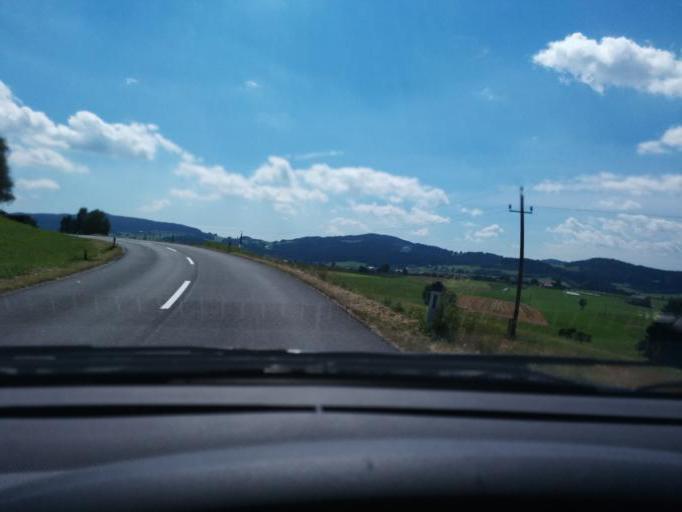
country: AT
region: Upper Austria
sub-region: Politischer Bezirk Rohrbach
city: Ulrichsberg
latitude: 48.6967
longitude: 13.9040
